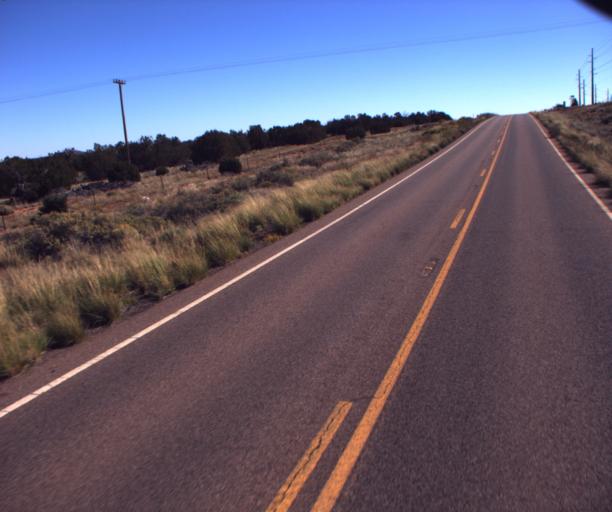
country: US
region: Arizona
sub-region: Navajo County
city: Taylor
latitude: 34.4827
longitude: -110.3091
